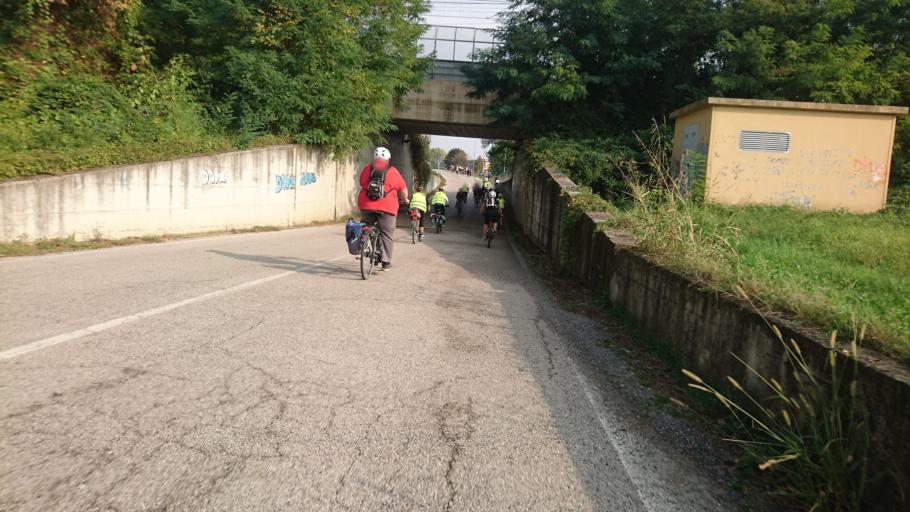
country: IT
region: Veneto
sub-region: Provincia di Rovigo
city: Arqua Polesine
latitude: 44.9971
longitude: 11.7430
